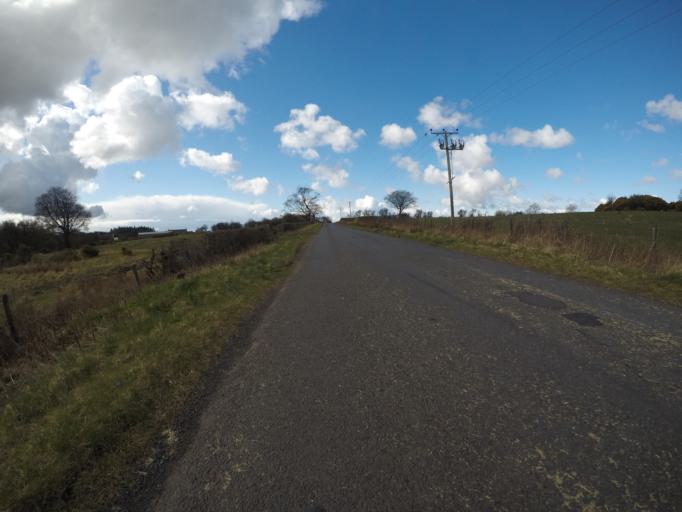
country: GB
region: Scotland
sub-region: North Ayrshire
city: Kilbirnie
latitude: 55.7159
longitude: -4.6831
